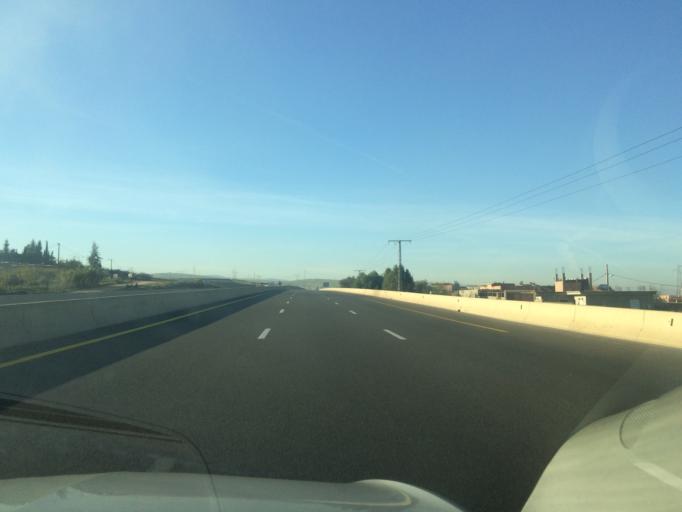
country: DZ
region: Chlef
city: Oued Sly
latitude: 36.0826
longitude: 1.1862
